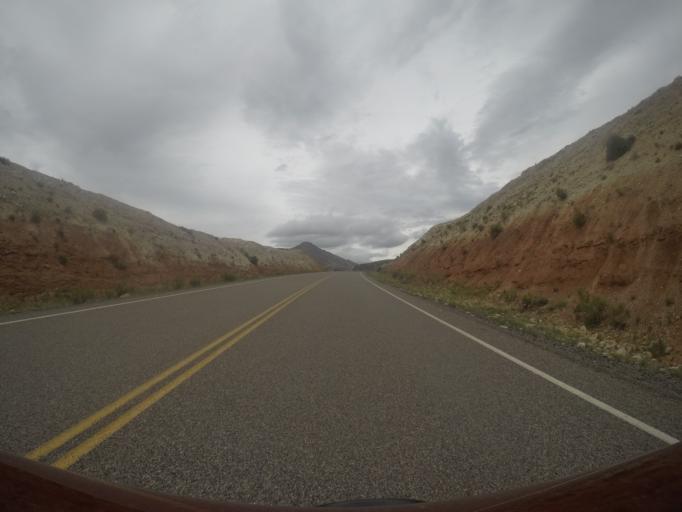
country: US
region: Wyoming
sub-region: Big Horn County
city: Lovell
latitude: 45.0047
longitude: -108.2684
